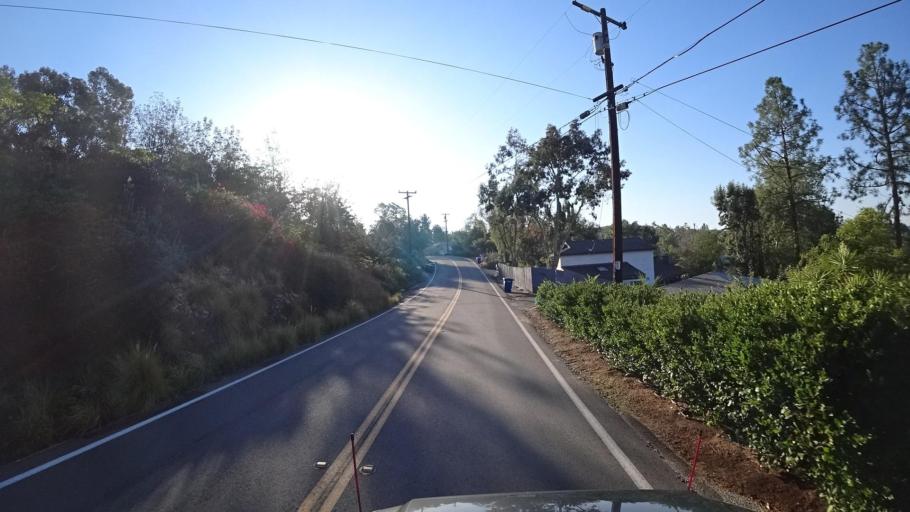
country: US
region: California
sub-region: San Diego County
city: Spring Valley
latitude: 32.7602
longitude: -116.9974
